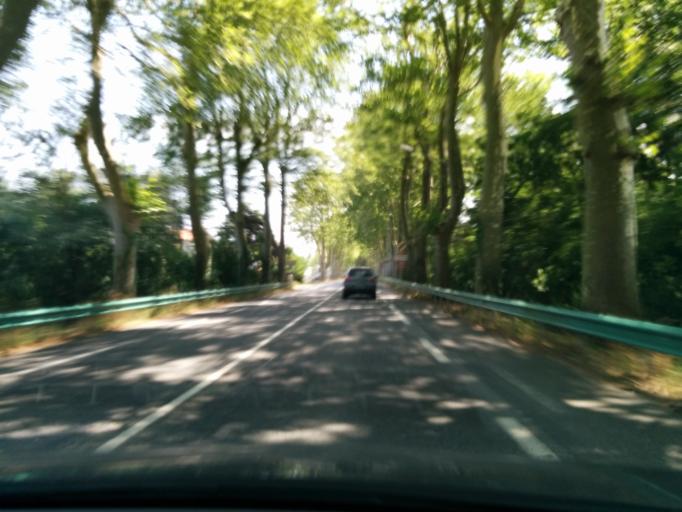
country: FR
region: Midi-Pyrenees
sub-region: Departement de la Haute-Garonne
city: Villefranche-de-Lauragais
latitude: 43.4096
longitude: 1.7058
